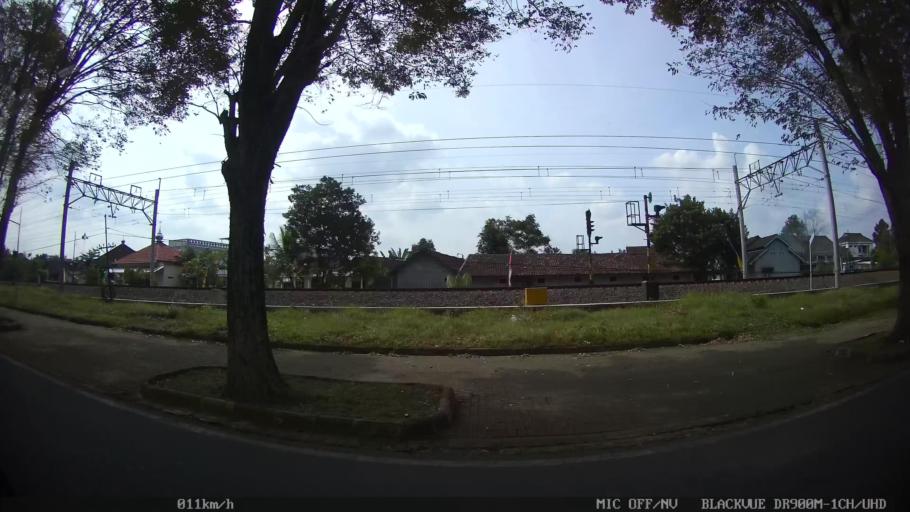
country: ID
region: Daerah Istimewa Yogyakarta
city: Depok
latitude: -7.7850
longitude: 110.4416
